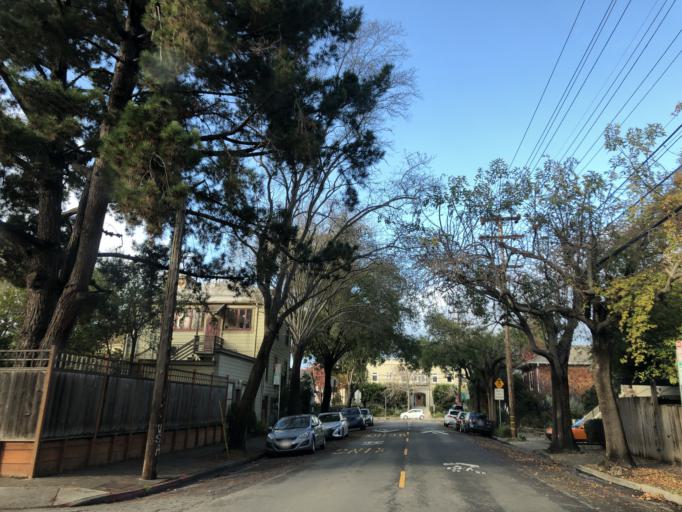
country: US
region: California
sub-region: Alameda County
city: Berkeley
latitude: 37.8499
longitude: -122.2568
